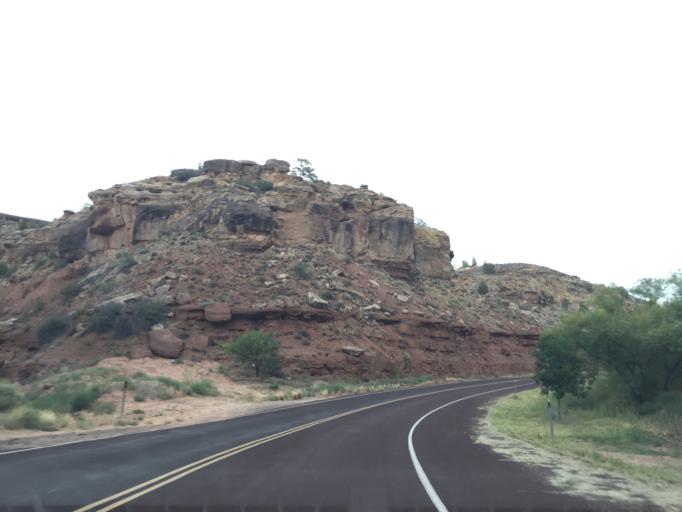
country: US
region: Utah
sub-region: Washington County
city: Hildale
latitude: 37.1630
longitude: -113.0247
